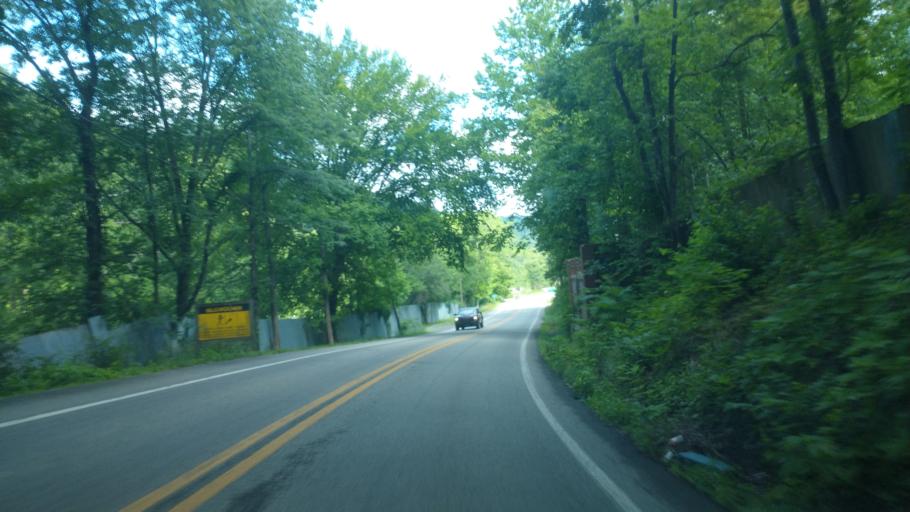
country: US
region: West Virginia
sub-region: McDowell County
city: Welch
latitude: 37.4180
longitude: -81.4952
